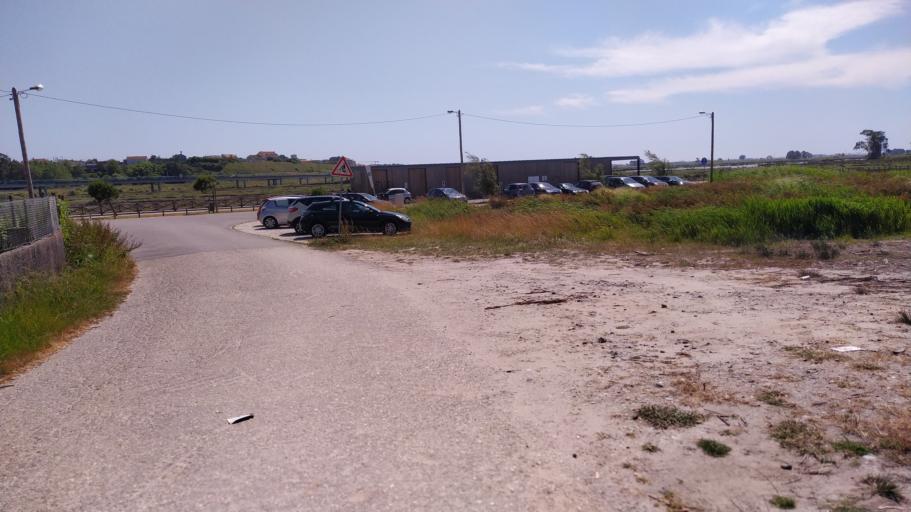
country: PT
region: Aveiro
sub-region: Aveiro
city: Aveiro
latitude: 40.6575
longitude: -8.6360
